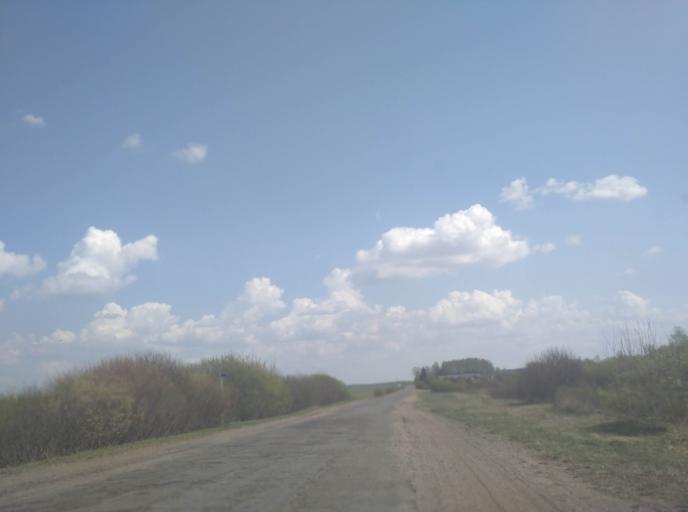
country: BY
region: Minsk
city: Loshnitsa
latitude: 54.4828
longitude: 28.7496
